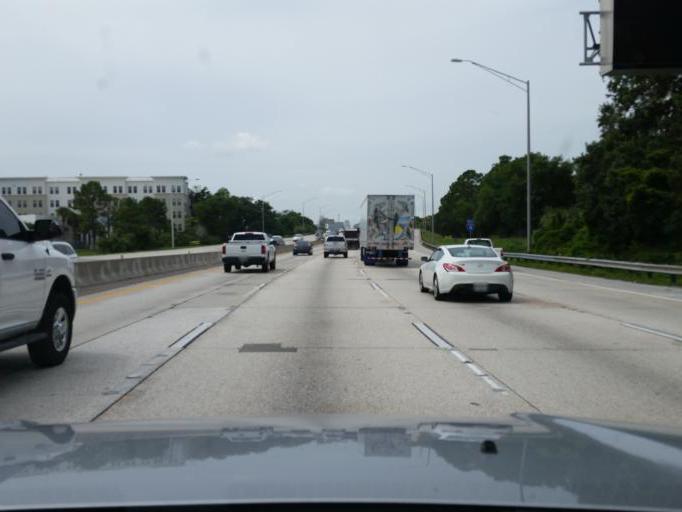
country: US
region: Florida
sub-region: Orange County
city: Fairview Shores
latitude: 28.5785
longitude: -81.3752
